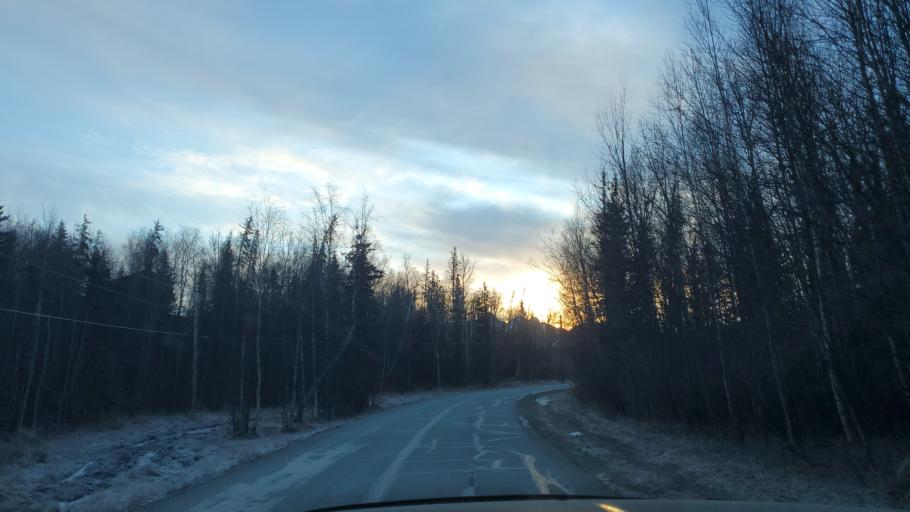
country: US
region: Alaska
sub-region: Matanuska-Susitna Borough
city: Lakes
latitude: 61.6027
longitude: -149.3170
